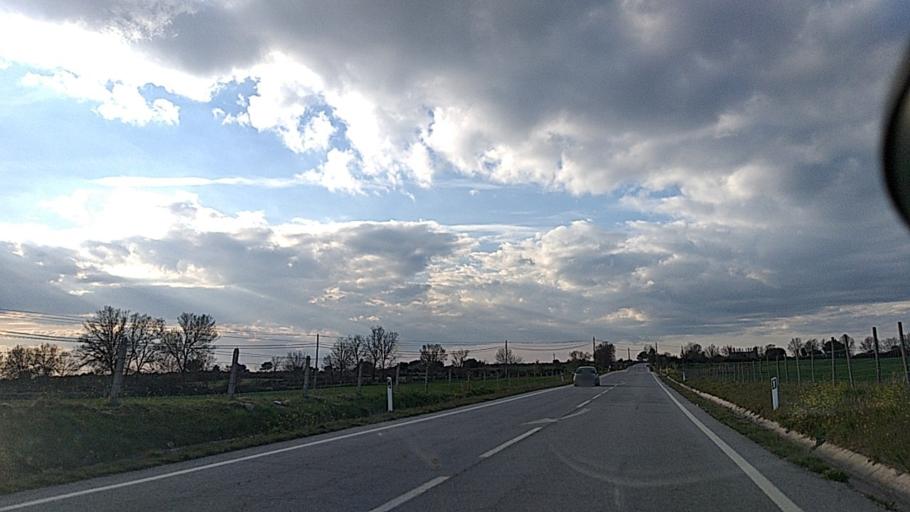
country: ES
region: Castille and Leon
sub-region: Provincia de Salamanca
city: Aldea del Obispo
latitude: 40.6955
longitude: -6.8836
